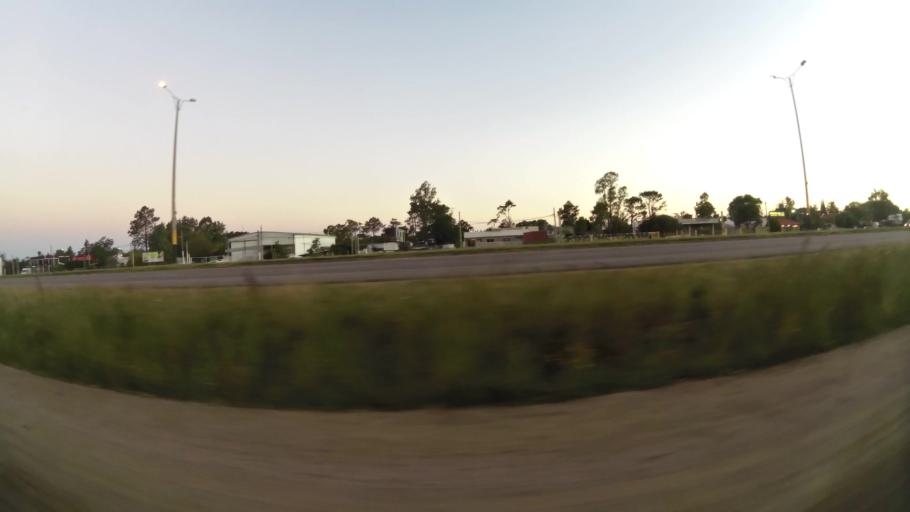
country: UY
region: Canelones
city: Colonia Nicolich
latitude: -34.8192
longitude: -55.9538
